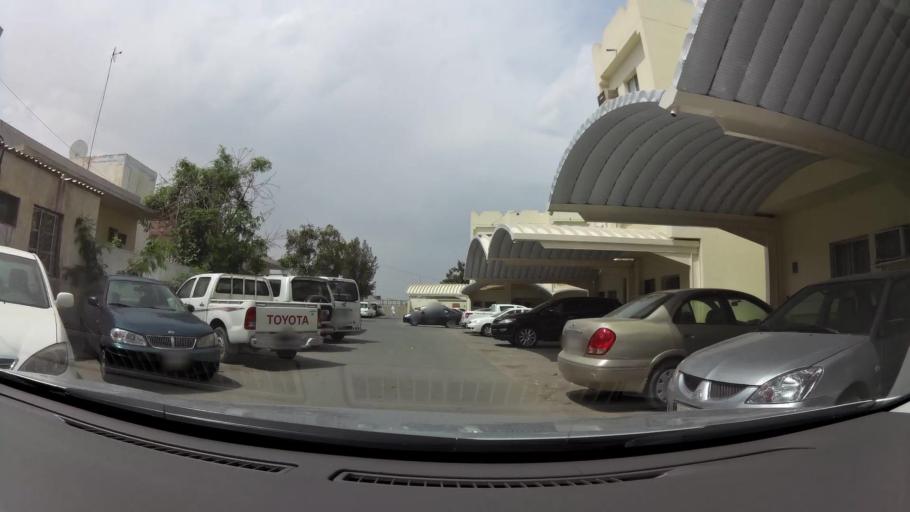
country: QA
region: Baladiyat ad Dawhah
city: Doha
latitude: 25.2766
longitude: 51.5207
